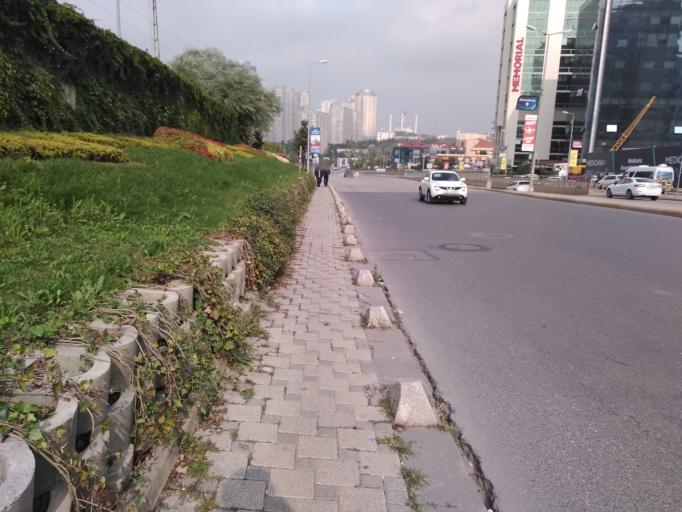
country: TR
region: Istanbul
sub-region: Atasehir
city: Atasehir
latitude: 40.9833
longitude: 29.1059
